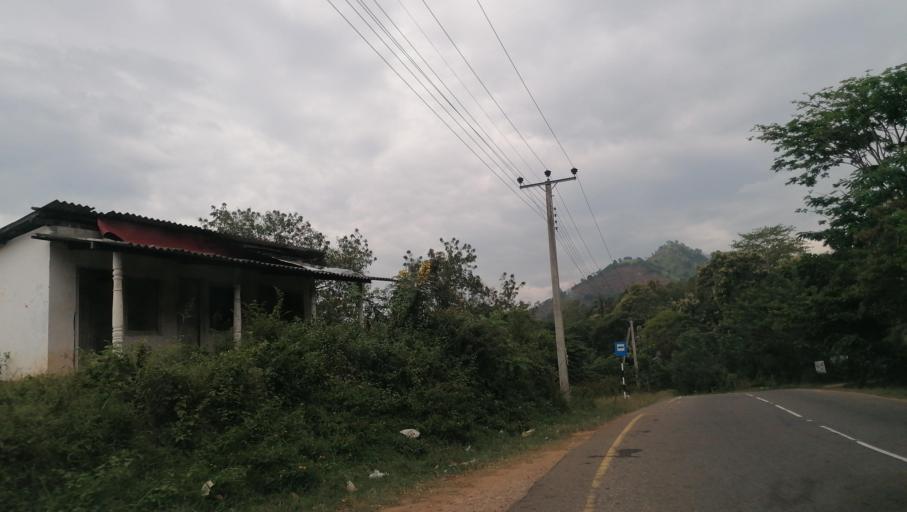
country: LK
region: Central
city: Kandy
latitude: 7.2225
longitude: 80.7642
